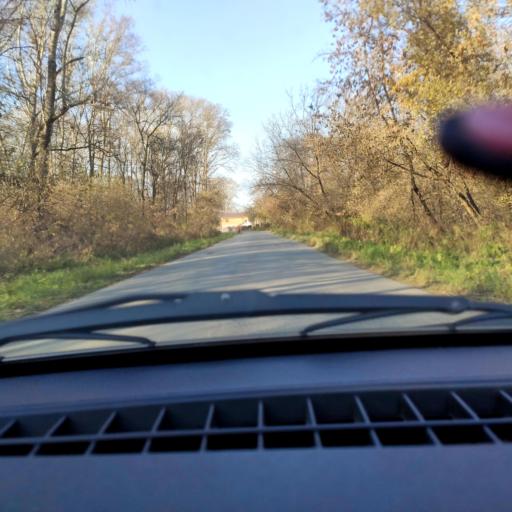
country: RU
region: Bashkortostan
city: Ufa
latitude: 54.7949
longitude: 56.1541
